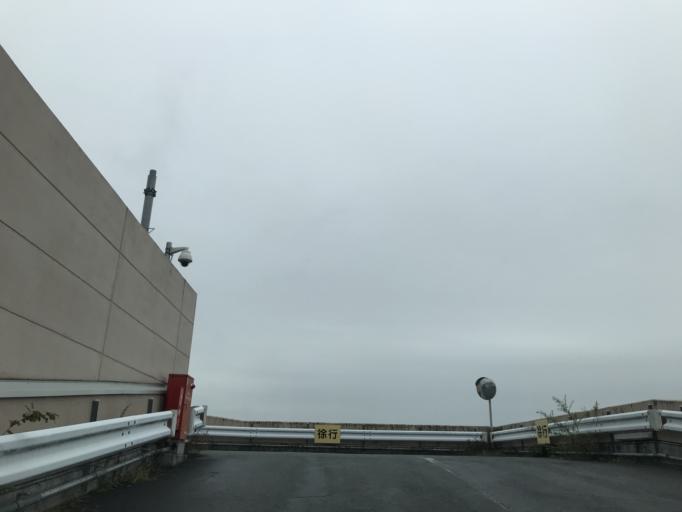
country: JP
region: Iwate
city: Ichinoseki
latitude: 38.9367
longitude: 141.1122
